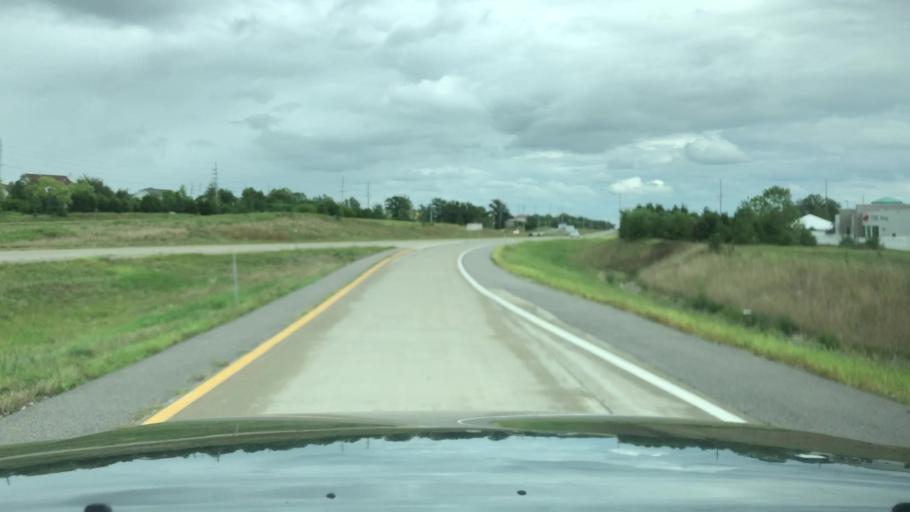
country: US
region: Missouri
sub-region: Saint Charles County
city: Dardenne Prairie
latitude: 38.7672
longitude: -90.7398
